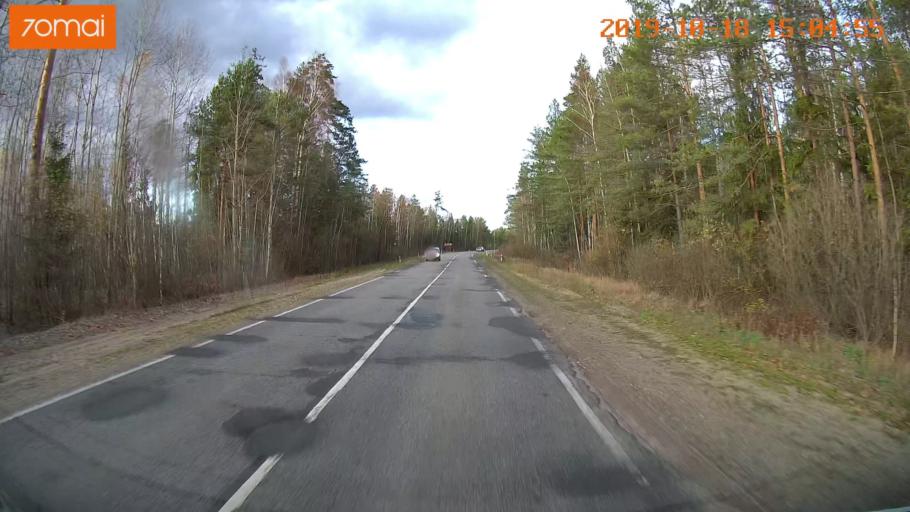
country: RU
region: Vladimir
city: Kurlovo
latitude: 55.5077
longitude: 40.5703
